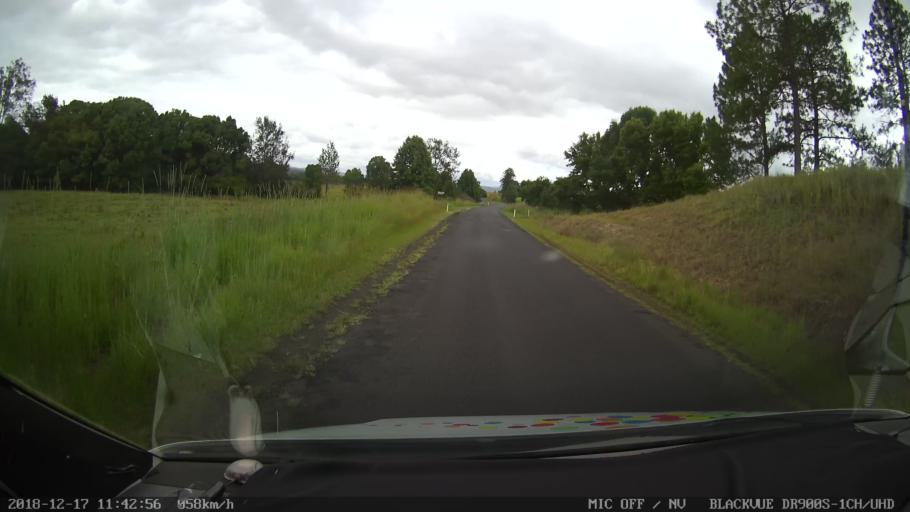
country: AU
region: New South Wales
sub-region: Kyogle
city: Kyogle
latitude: -28.6643
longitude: 152.5926
